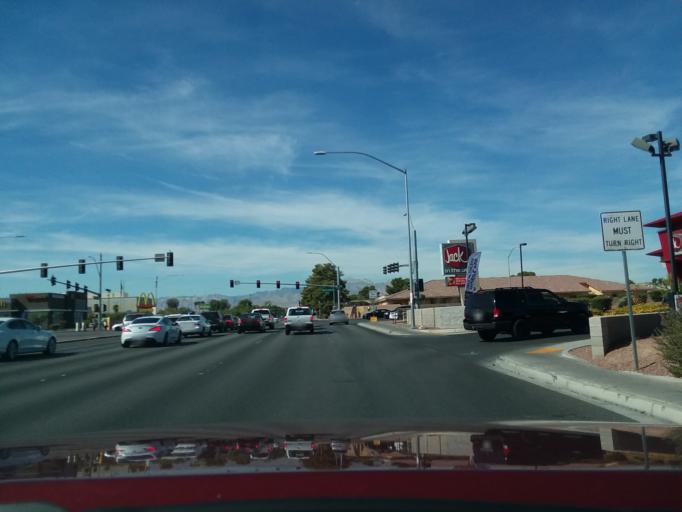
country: US
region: Nevada
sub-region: Clark County
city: Las Vegas
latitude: 36.1958
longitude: -115.1599
